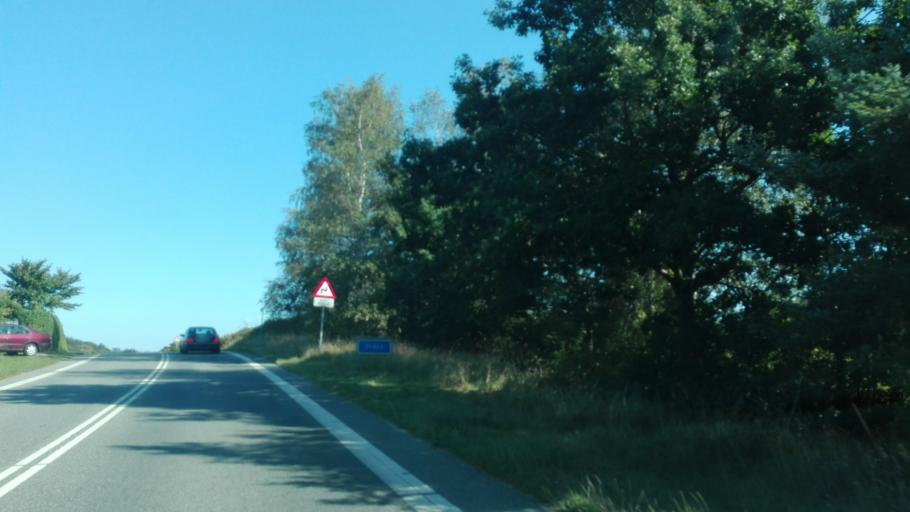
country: DK
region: Central Jutland
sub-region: Syddjurs Kommune
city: Ebeltoft
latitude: 56.2200
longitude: 10.6990
